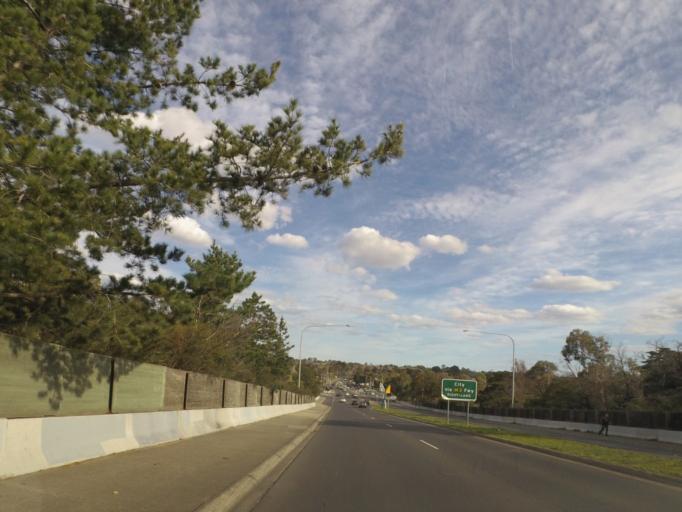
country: AU
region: Victoria
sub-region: Manningham
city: Doncaster East
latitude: -37.7958
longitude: 145.1424
